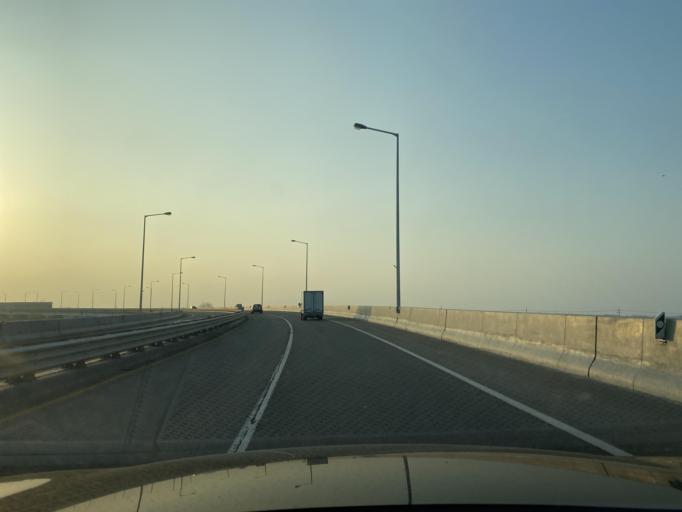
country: KR
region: Chungcheongnam-do
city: Yesan
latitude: 36.7046
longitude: 126.8261
